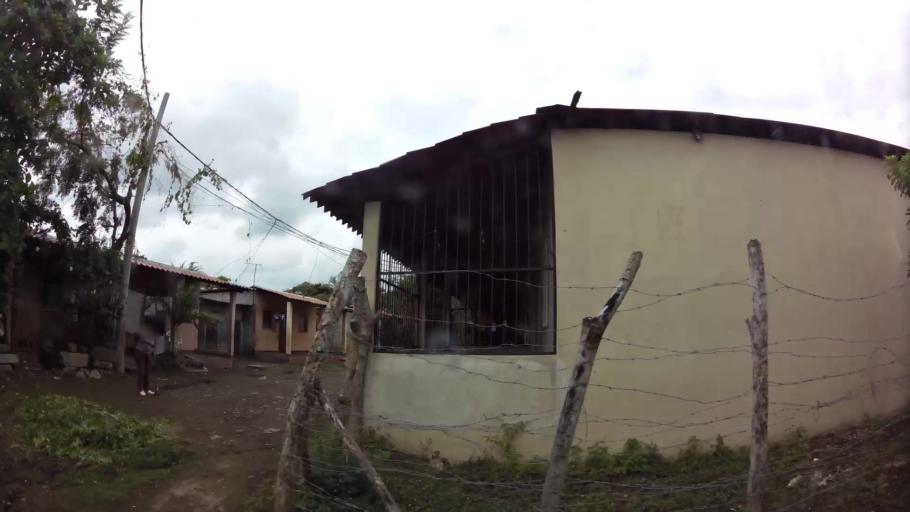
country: NI
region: Granada
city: Granada
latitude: 11.9352
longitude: -85.9448
